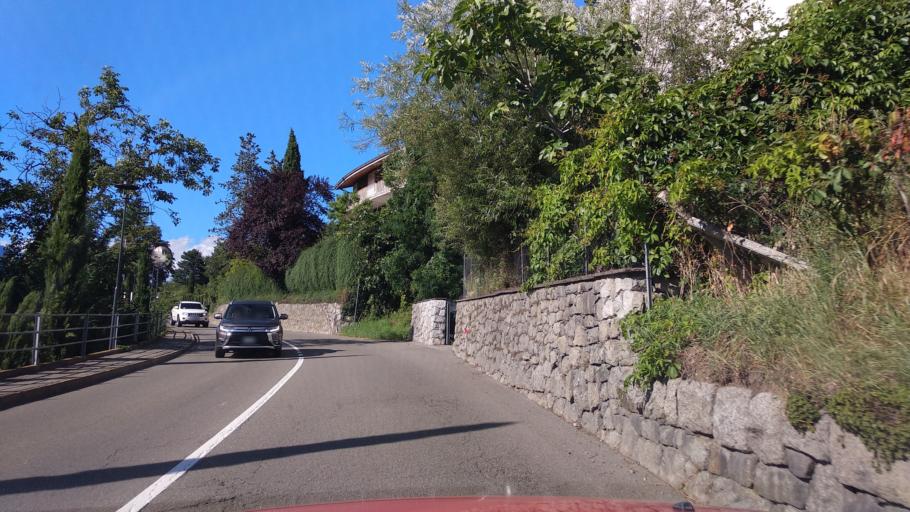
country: IT
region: Trentino-Alto Adige
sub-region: Bolzano
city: Scena
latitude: 46.6761
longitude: 11.1889
